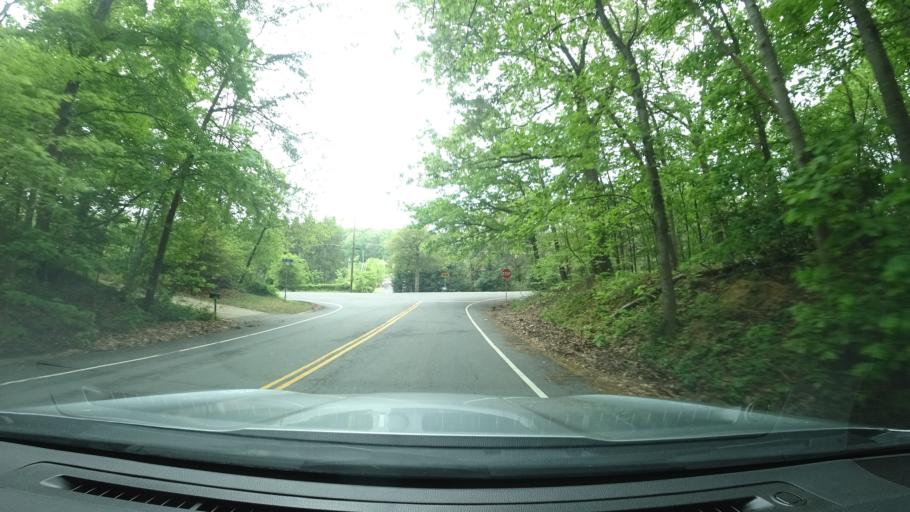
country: US
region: Virginia
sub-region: Fairfax County
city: Oak Hill
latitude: 38.9177
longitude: -77.3666
